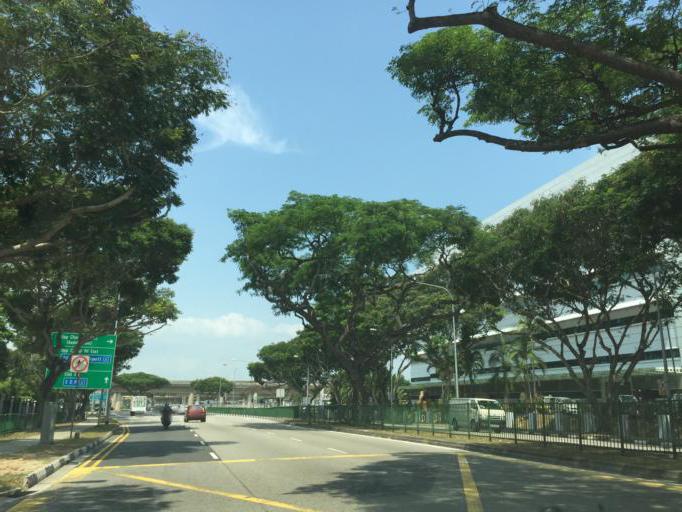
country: SG
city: Singapore
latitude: 1.3337
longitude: 103.9538
